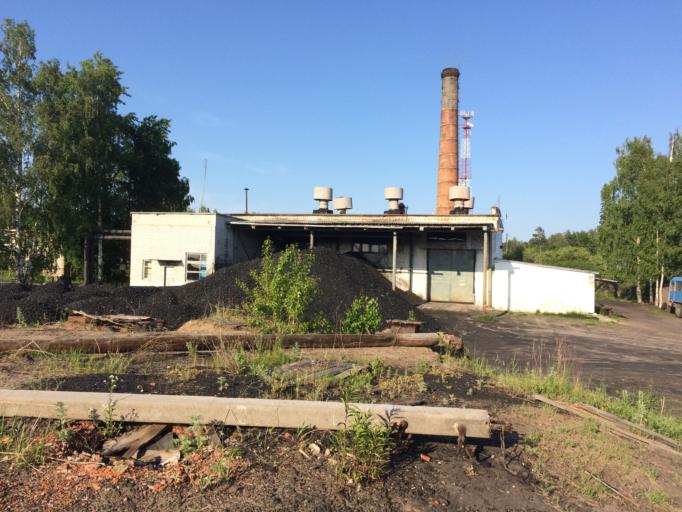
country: RU
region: Mariy-El
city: Mochalishche
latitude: 56.5420
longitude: 48.4020
